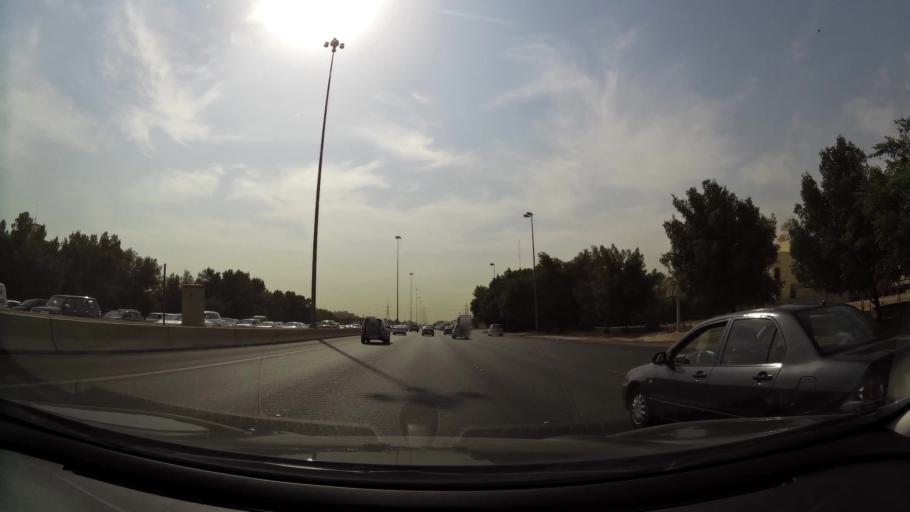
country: KW
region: Al Asimah
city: Ash Shamiyah
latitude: 29.3124
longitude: 47.9762
